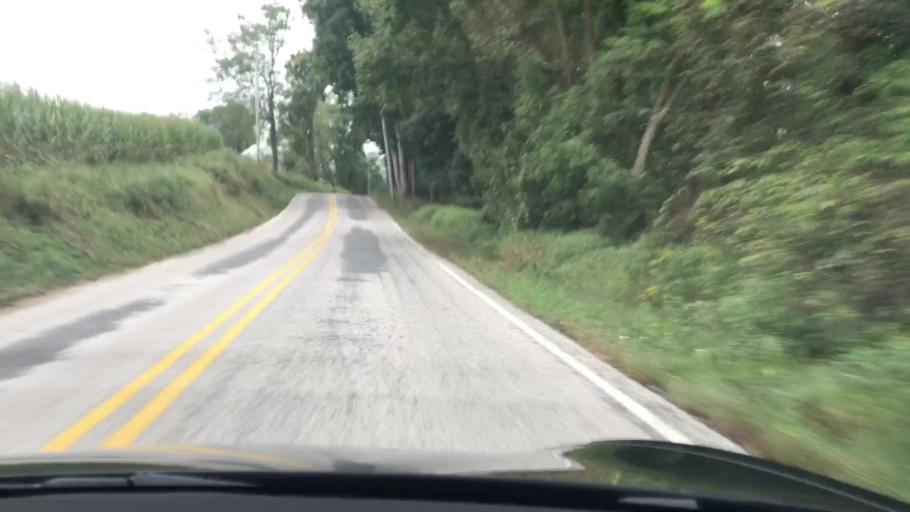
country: US
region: Pennsylvania
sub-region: York County
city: Dillsburg
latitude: 40.0597
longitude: -77.0703
